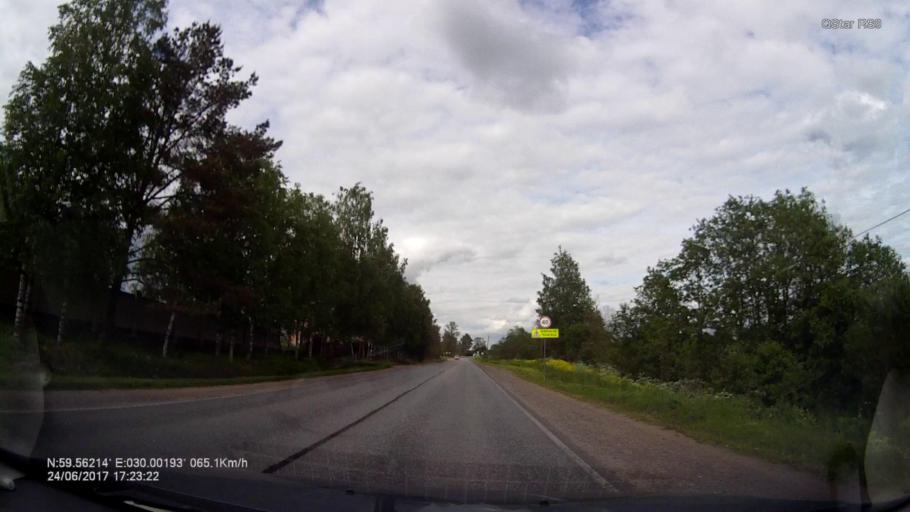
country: RU
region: Leningrad
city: Voyskovitsy
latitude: 59.5623
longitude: 30.0024
